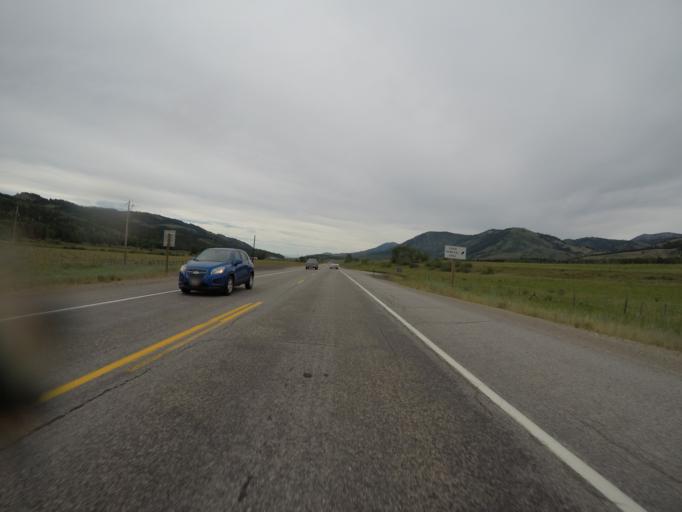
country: US
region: Wyoming
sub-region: Lincoln County
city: Afton
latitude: 42.5457
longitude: -110.8935
